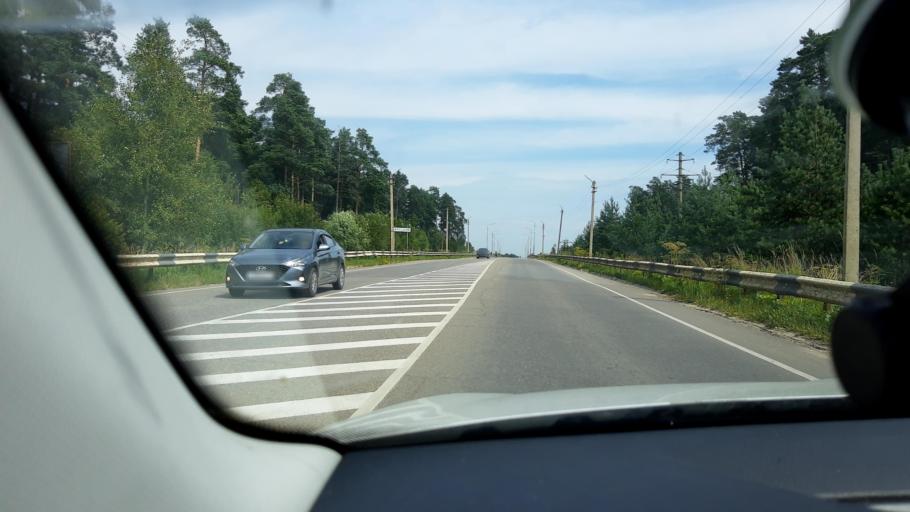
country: RU
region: Tula
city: Zaokskiy
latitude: 54.7435
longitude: 37.3885
